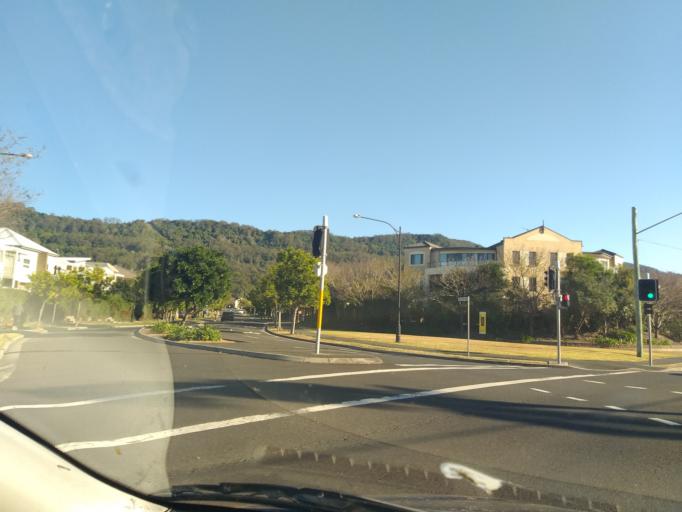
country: AU
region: New South Wales
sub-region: Wollongong
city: Bulli
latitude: -34.3485
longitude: 150.9039
